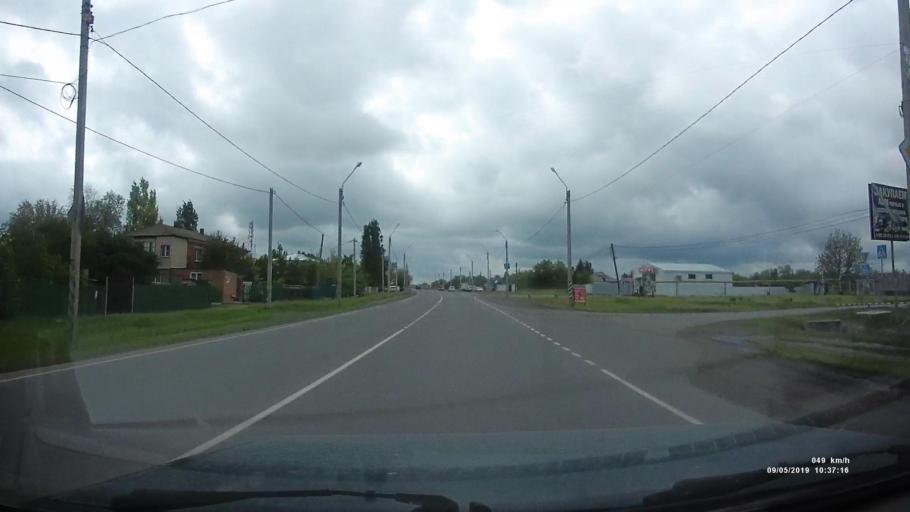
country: RU
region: Rostov
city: Peshkovo
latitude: 47.0217
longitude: 39.4040
